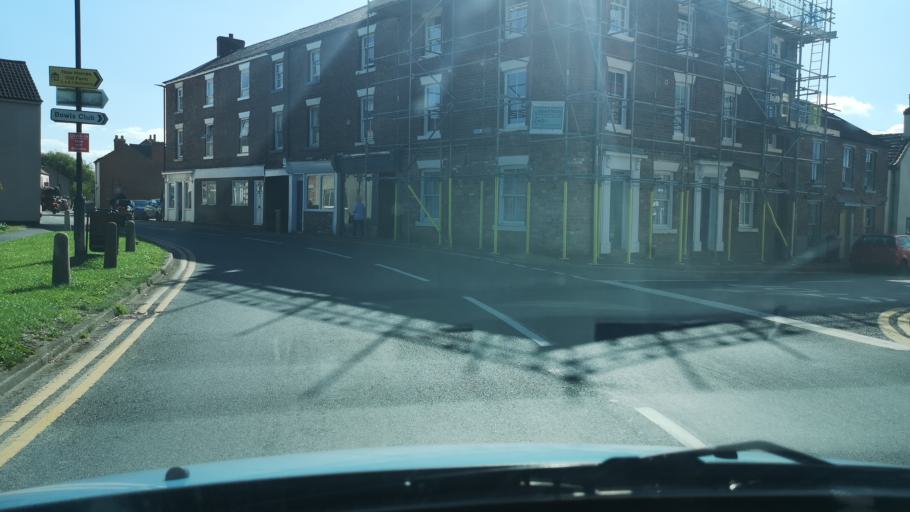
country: GB
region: England
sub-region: North Lincolnshire
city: Crowle
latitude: 53.6090
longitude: -0.8334
